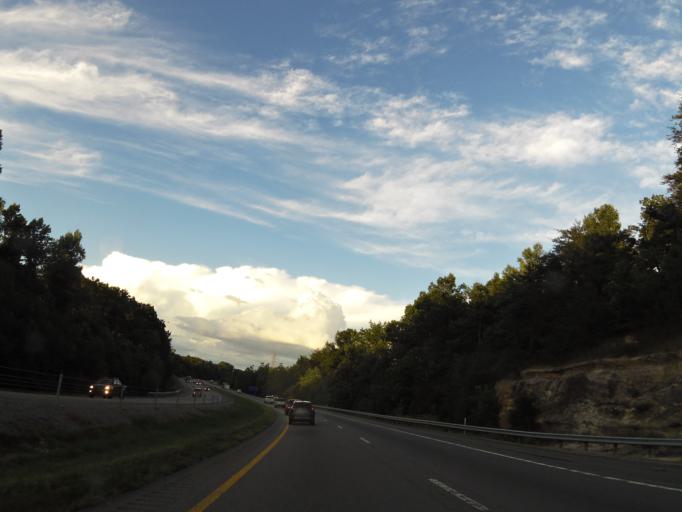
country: US
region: Tennessee
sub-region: Putnam County
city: Monterey
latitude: 36.1363
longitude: -85.3143
